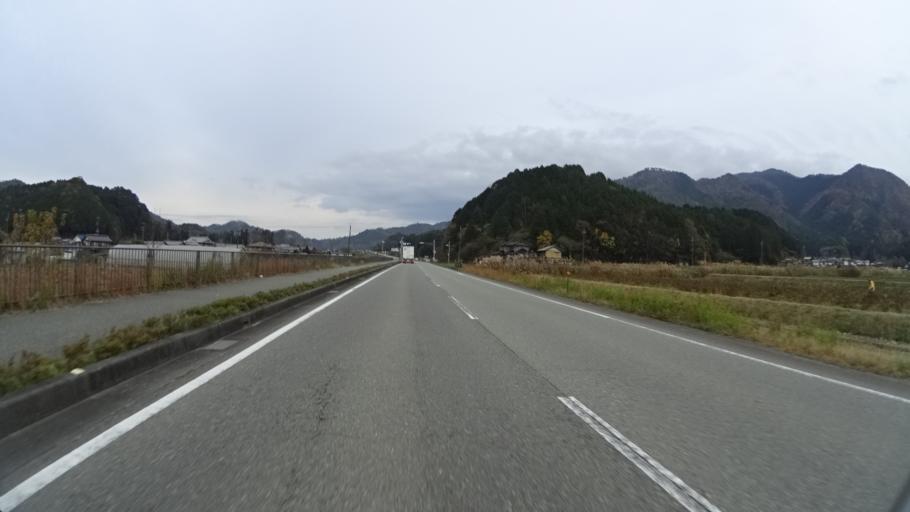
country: JP
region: Hyogo
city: Sasayama
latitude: 35.0683
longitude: 135.2951
